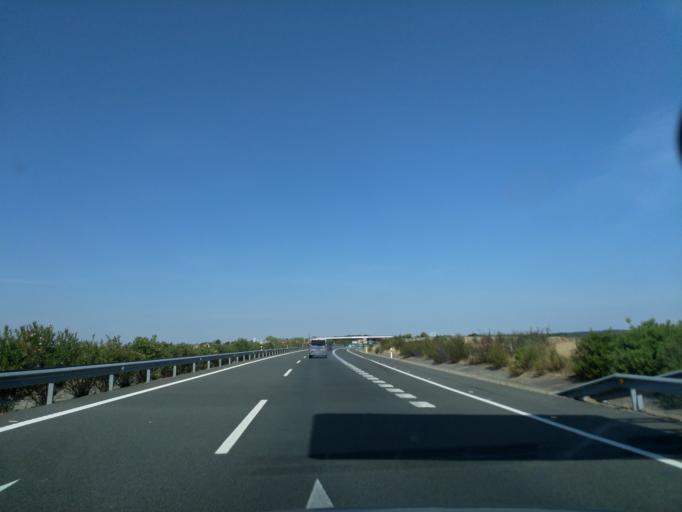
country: ES
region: Extremadura
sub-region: Provincia de Caceres
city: Casas de Don Antonio
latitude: 39.2255
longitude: -6.2998
